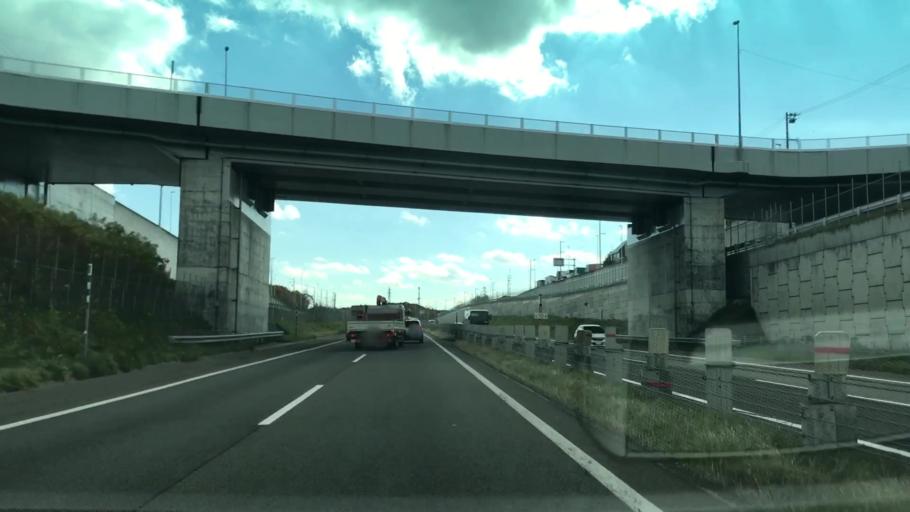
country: JP
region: Hokkaido
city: Kitahiroshima
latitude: 42.9931
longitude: 141.4693
